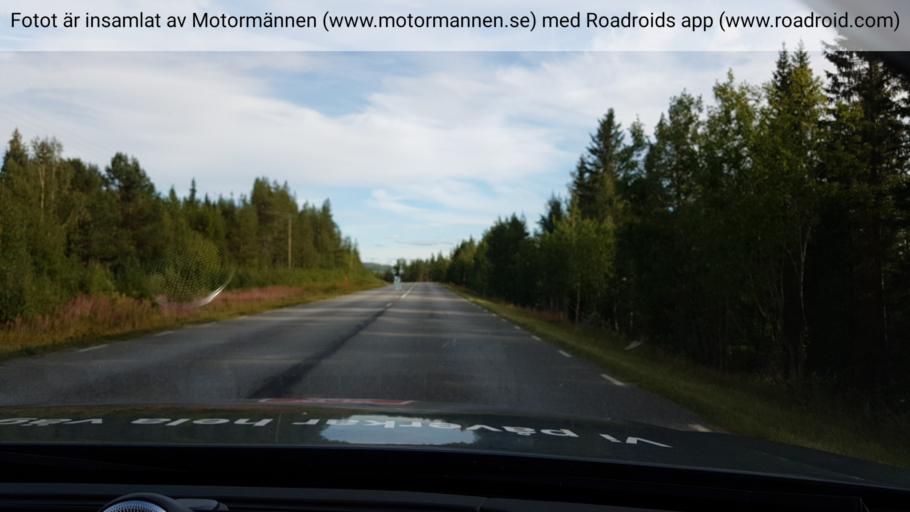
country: SE
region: Jaemtland
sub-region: Stroemsunds Kommun
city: Stroemsund
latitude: 64.2623
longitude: 15.3969
